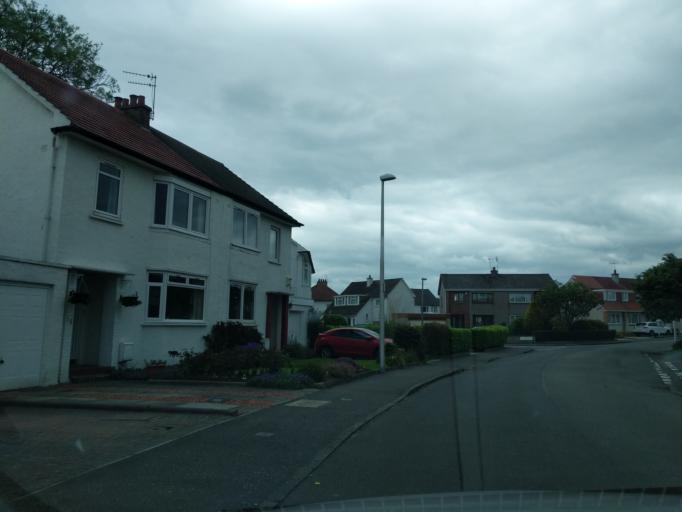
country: GB
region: Scotland
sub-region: Edinburgh
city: Colinton
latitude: 55.9702
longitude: -3.2694
